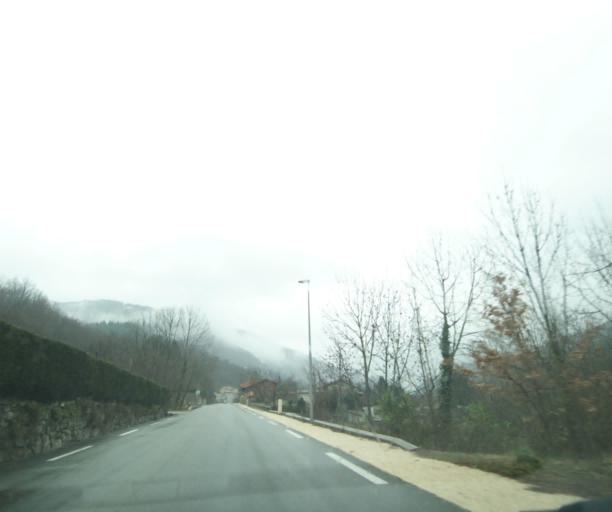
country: FR
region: Rhone-Alpes
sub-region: Departement de l'Ardeche
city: Thueyts
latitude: 44.6690
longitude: 4.1749
